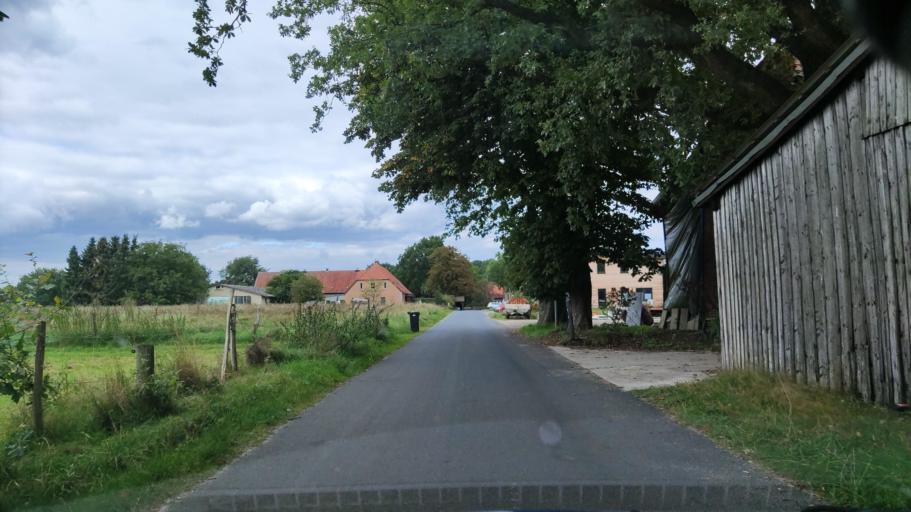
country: DE
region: Lower Saxony
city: Bispingen
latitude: 53.1394
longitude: 10.0219
